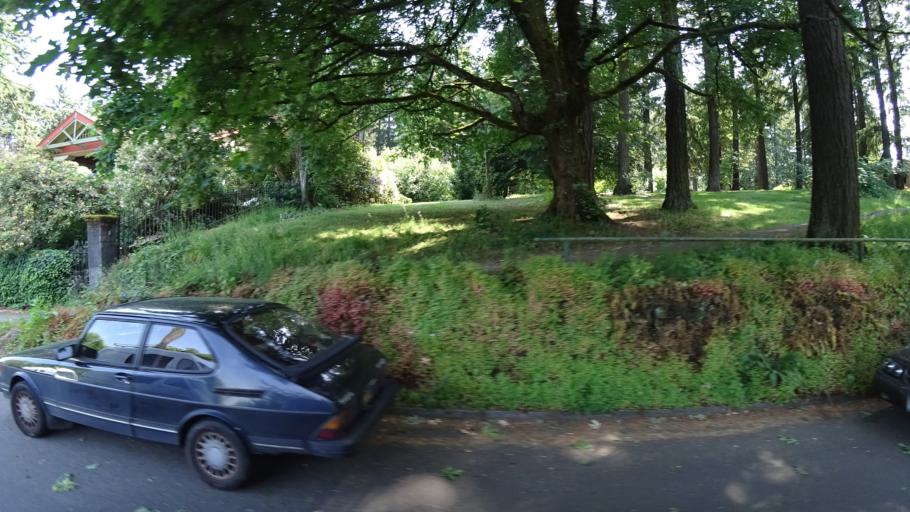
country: US
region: Oregon
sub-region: Multnomah County
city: Lents
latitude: 45.5161
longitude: -122.5948
